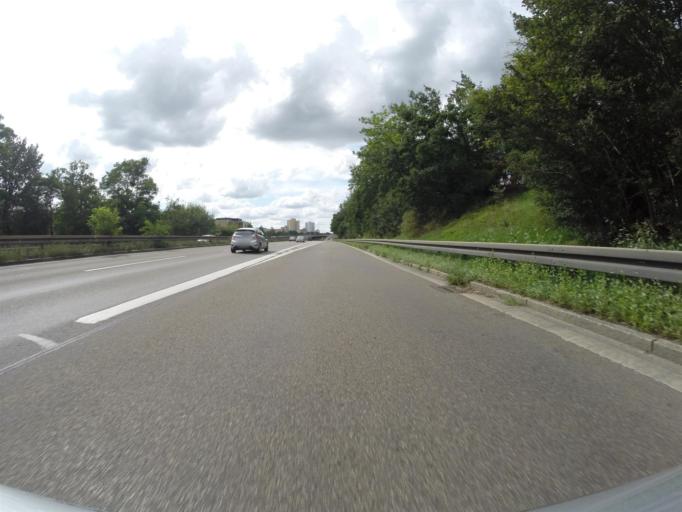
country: DE
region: Bavaria
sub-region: Regierungsbezirk Mittelfranken
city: Grossreuth bei Schweinau
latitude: 49.4214
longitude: 11.0432
